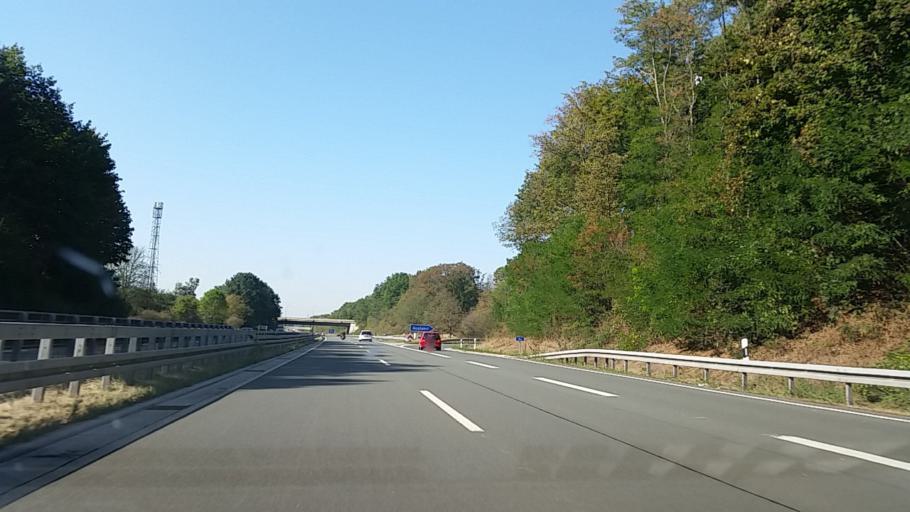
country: DE
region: North Rhine-Westphalia
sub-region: Regierungsbezirk Dusseldorf
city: Langenfeld
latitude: 51.0950
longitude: 6.9545
